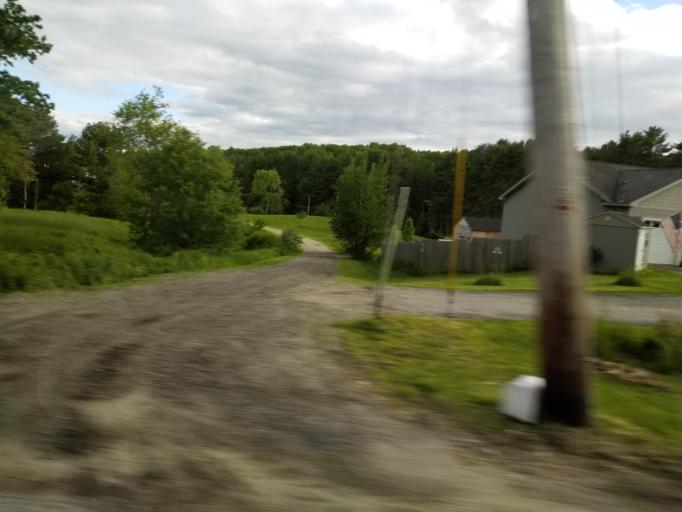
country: US
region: Maine
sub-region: Cumberland County
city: New Gloucester
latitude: 43.8935
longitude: -70.2845
